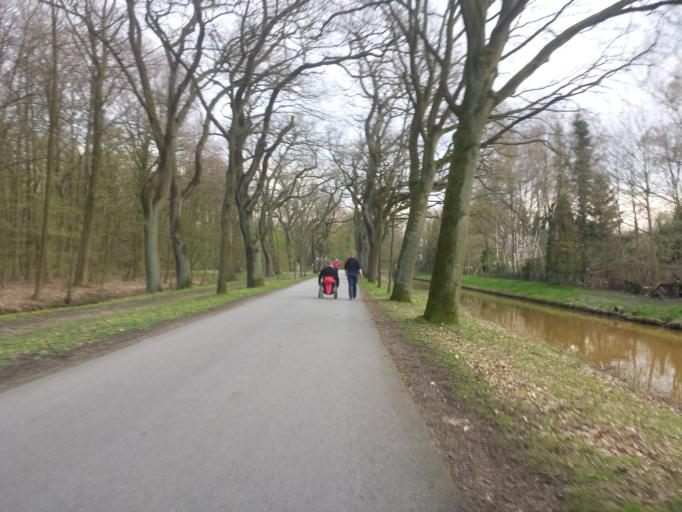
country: DE
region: Bremen
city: Bremen
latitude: 53.1046
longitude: 8.8245
